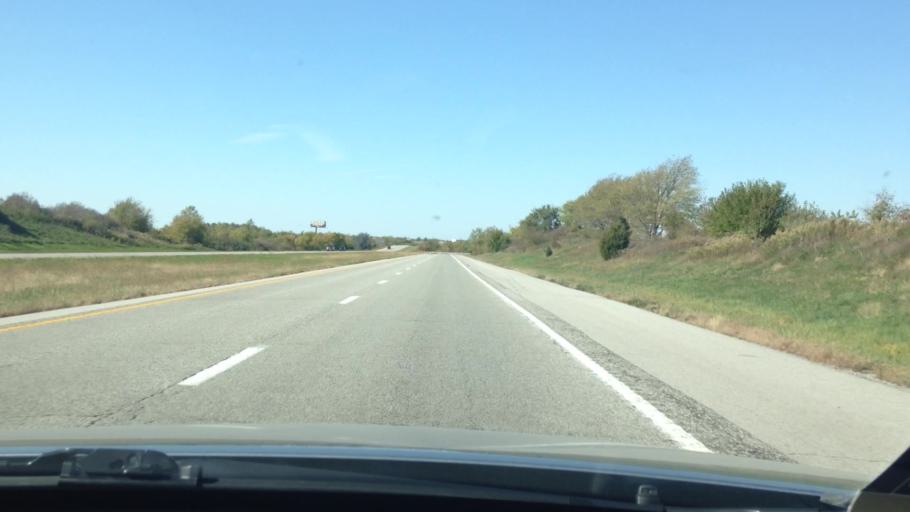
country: US
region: Missouri
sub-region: Platte County
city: Weatherby Lake
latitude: 39.3169
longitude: -94.6846
